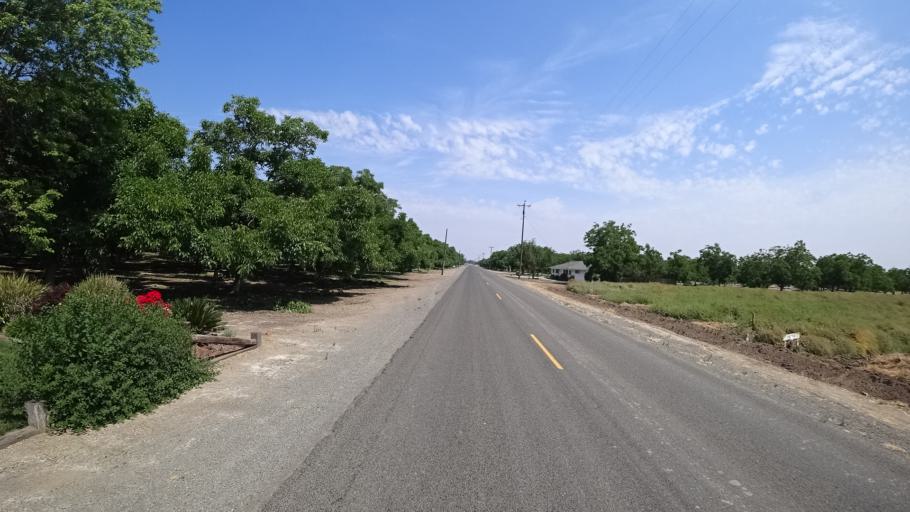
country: US
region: California
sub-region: Fresno County
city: Laton
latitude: 36.3964
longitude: -119.7450
